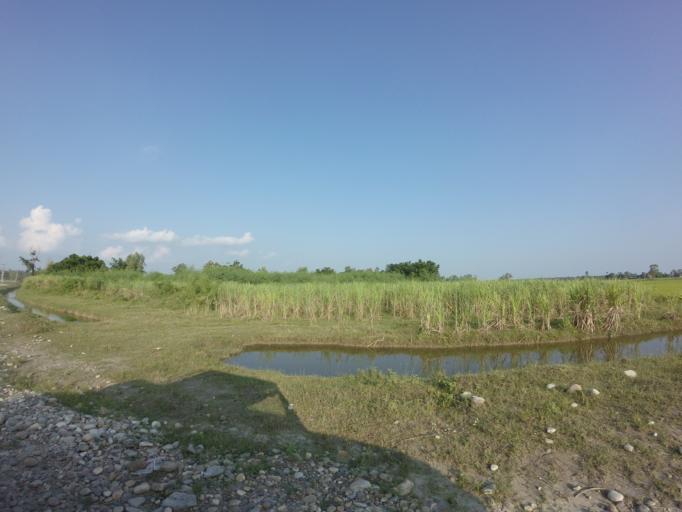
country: NP
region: Far Western
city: Tikapur
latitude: 28.4407
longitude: 81.0700
